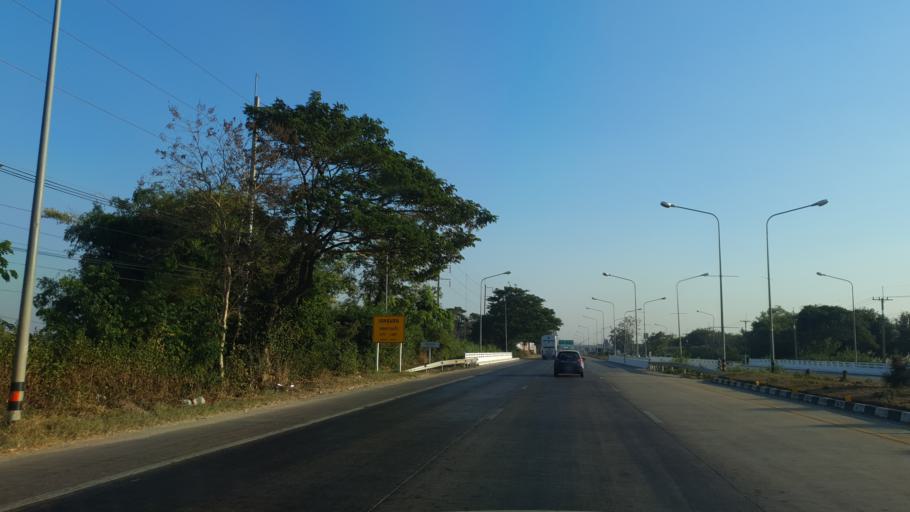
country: TH
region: Kamphaeng Phet
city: Khlong Khlung
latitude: 16.2197
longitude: 99.7008
